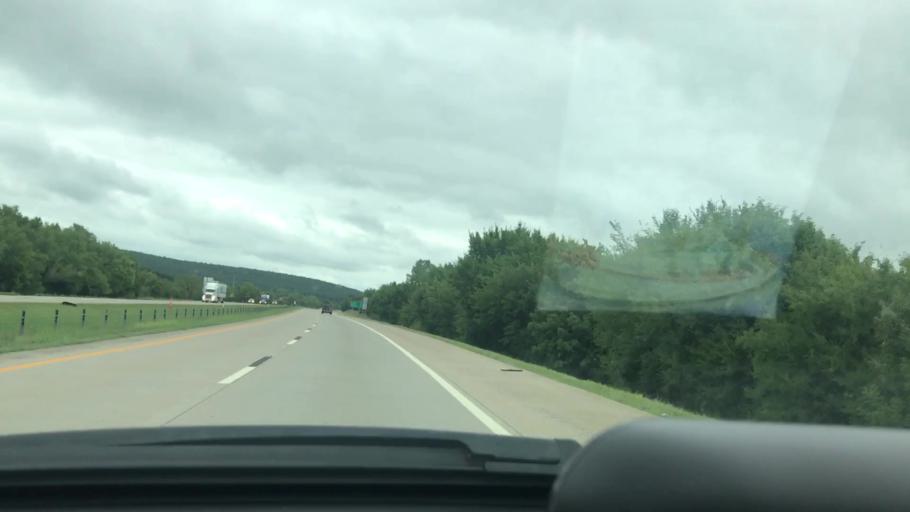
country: US
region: Oklahoma
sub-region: Pittsburg County
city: Krebs
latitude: 35.0077
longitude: -95.7187
